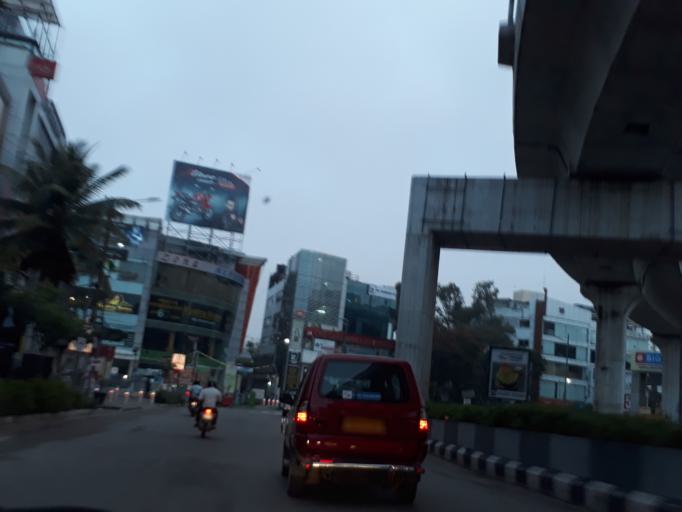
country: IN
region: Telangana
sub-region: Rangareddi
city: Kukatpalli
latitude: 17.4312
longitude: 78.4074
